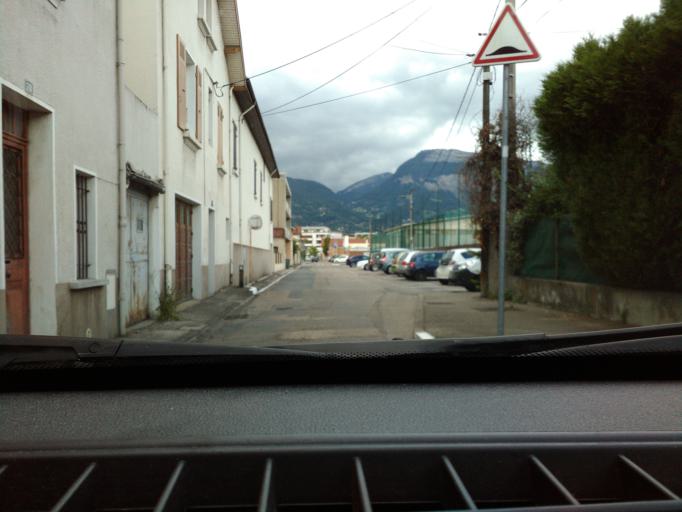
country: FR
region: Rhone-Alpes
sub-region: Departement de l'Isere
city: Saint-Martin-d'Heres
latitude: 45.1821
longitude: 5.7508
